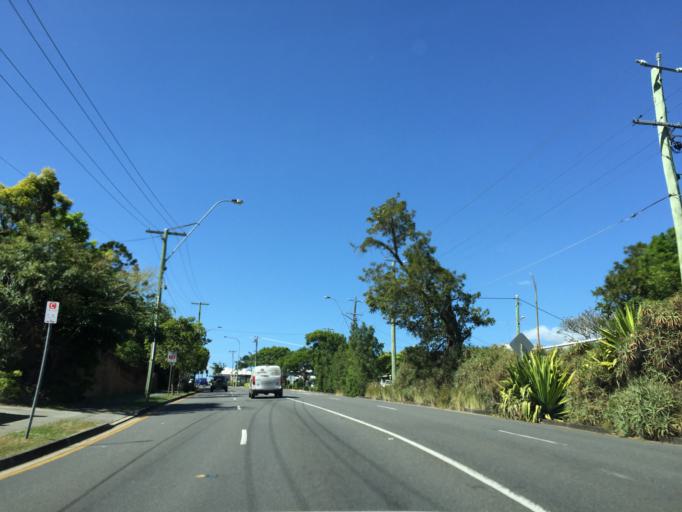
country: AU
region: Queensland
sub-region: Brisbane
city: Milton
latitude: -27.4511
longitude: 153.0014
